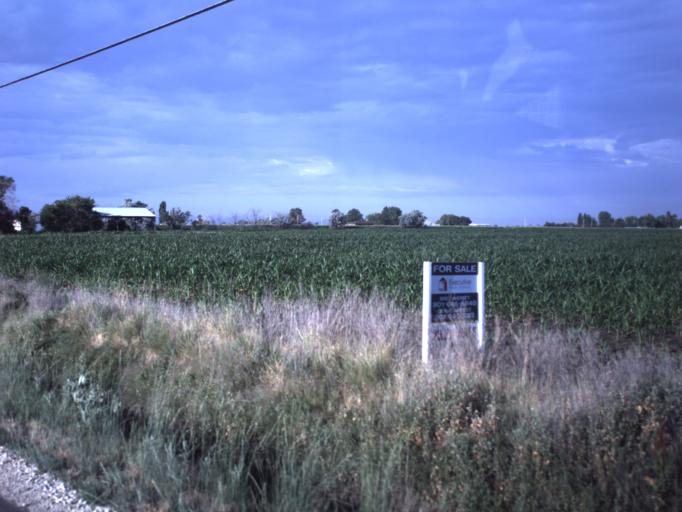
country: US
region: Utah
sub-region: Weber County
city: Plain City
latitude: 41.2506
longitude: -112.0926
